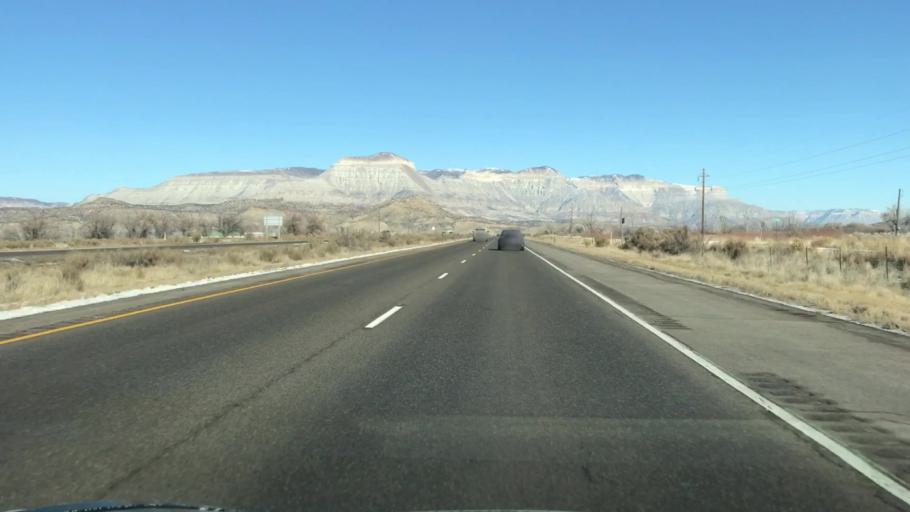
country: US
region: Colorado
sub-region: Garfield County
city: Parachute
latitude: 39.3087
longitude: -108.2154
